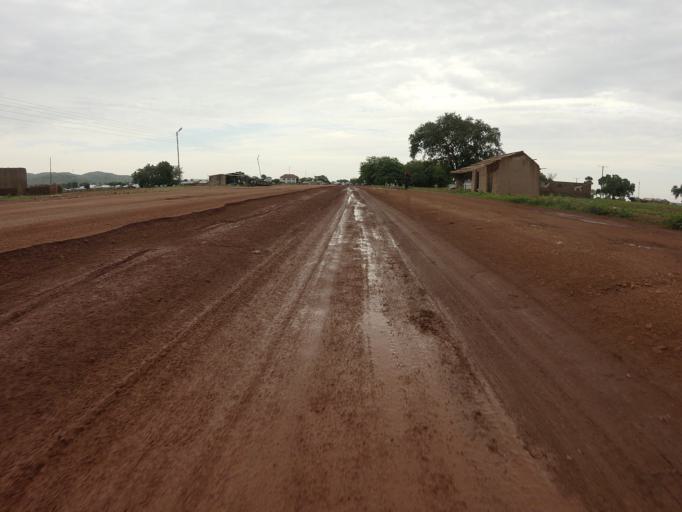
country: GH
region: Upper East
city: Bawku
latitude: 10.9306
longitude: -0.5022
